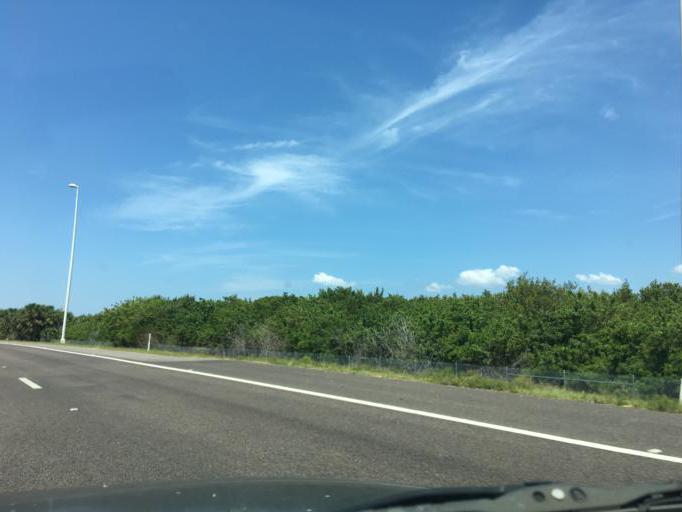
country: US
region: Florida
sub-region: Hillsborough County
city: Town 'n' Country
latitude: 27.9457
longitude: -82.5400
